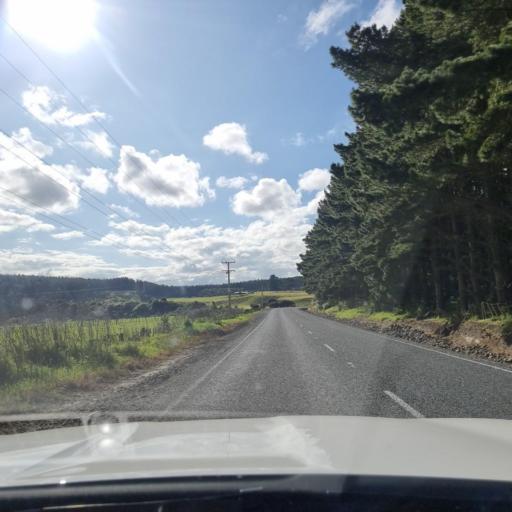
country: NZ
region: Northland
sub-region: Kaipara District
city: Dargaville
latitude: -36.2541
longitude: 174.0437
